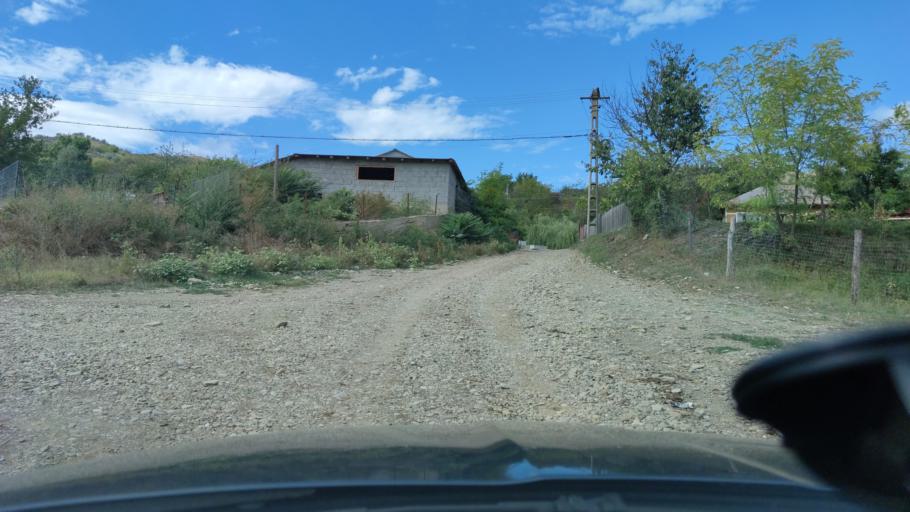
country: RO
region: Buzau
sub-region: Comuna Beceni
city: Valea Parului
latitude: 45.3601
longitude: 26.7682
